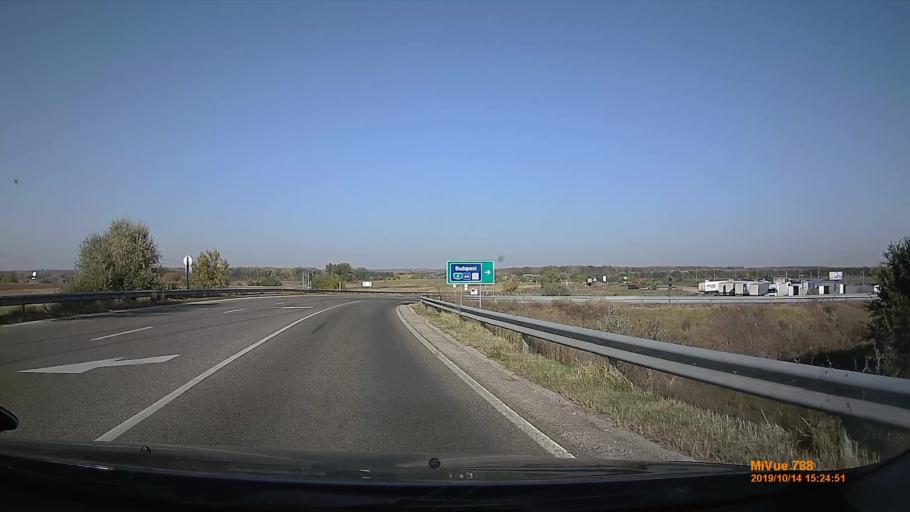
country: HU
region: Pest
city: Vecses
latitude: 47.4059
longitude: 19.3040
